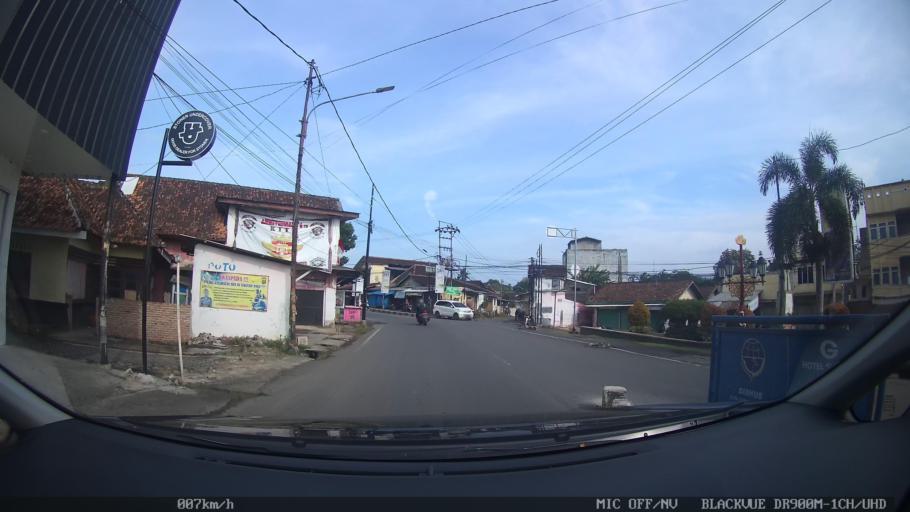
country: ID
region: Lampung
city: Kedaton
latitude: -5.3867
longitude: 105.2669
